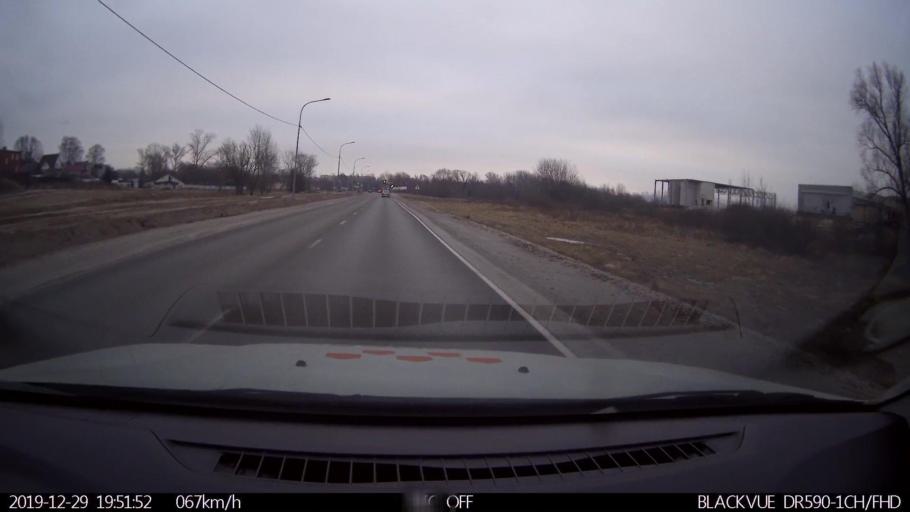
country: RU
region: Nizjnij Novgorod
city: Bor
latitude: 56.3577
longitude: 44.0477
